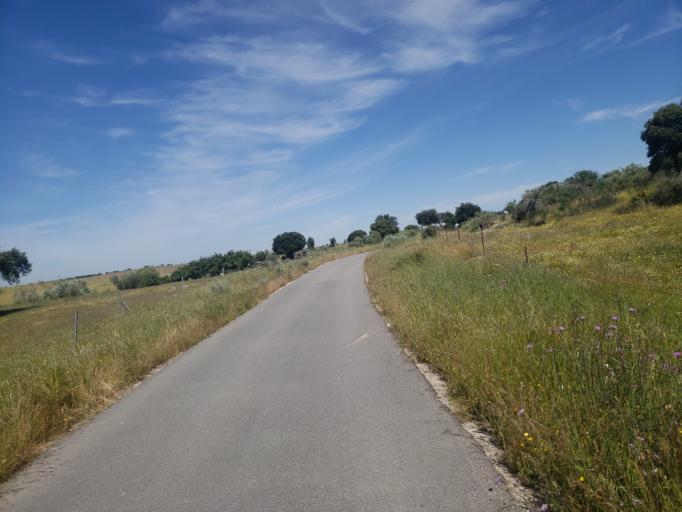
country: ES
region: Extremadura
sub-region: Provincia de Caceres
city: Malpartida de Caceres
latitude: 39.4182
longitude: -6.5048
